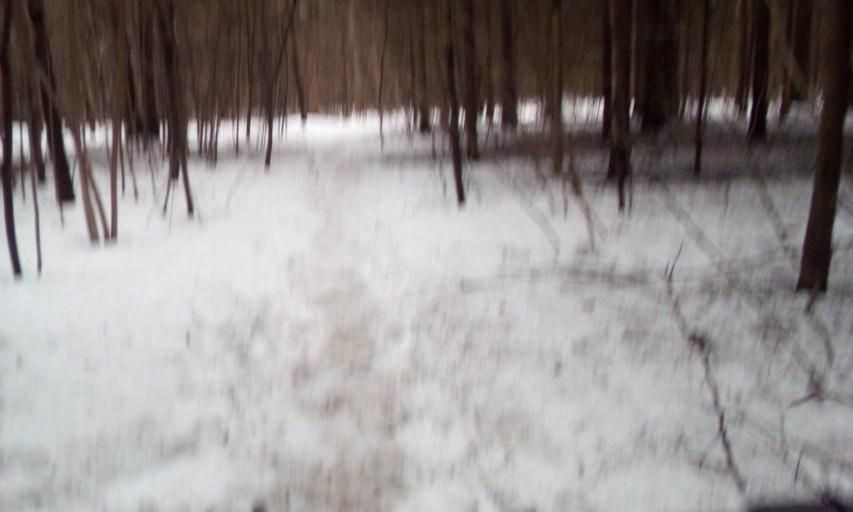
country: RU
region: Moskovskaya
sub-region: Leninskiy Rayon
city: Vnukovo
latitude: 55.6328
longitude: 37.2812
